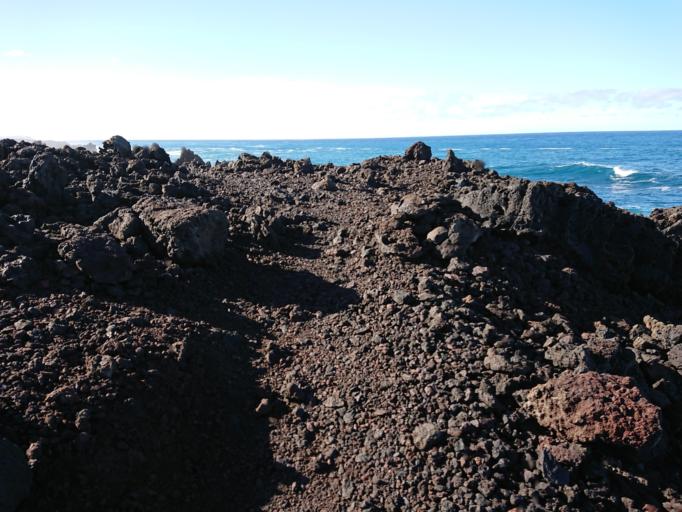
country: ES
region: Canary Islands
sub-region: Provincia de Las Palmas
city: Tinajo
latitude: 29.0810
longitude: -13.7338
